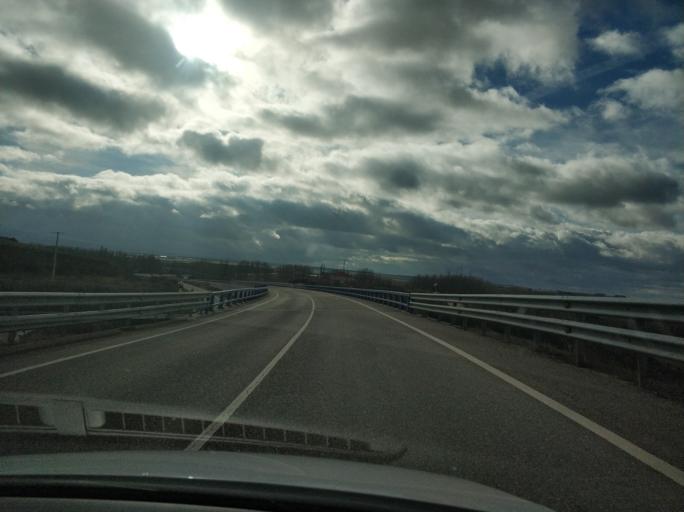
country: ES
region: Castille and Leon
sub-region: Provincia de Segovia
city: Ayllon
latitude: 41.4175
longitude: -3.4069
